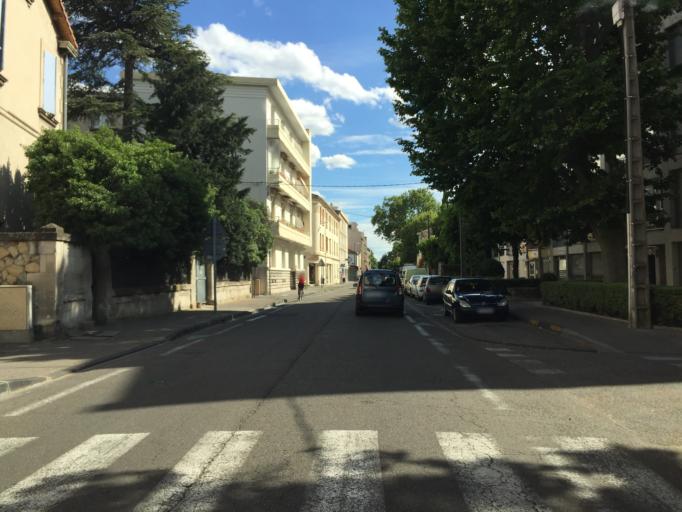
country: FR
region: Provence-Alpes-Cote d'Azur
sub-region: Departement du Vaucluse
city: Avignon
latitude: 43.9387
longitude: 4.8056
